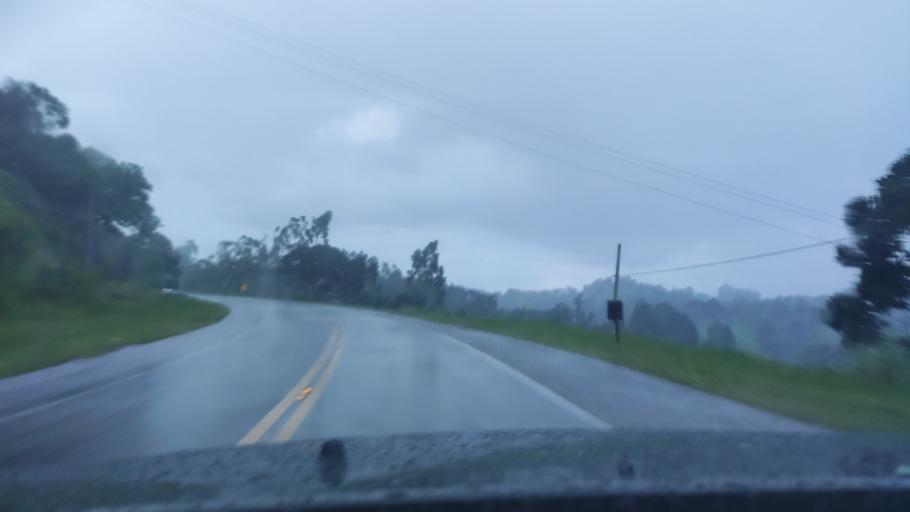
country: BR
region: Sao Paulo
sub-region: Socorro
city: Socorro
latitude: -22.7679
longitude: -46.5576
